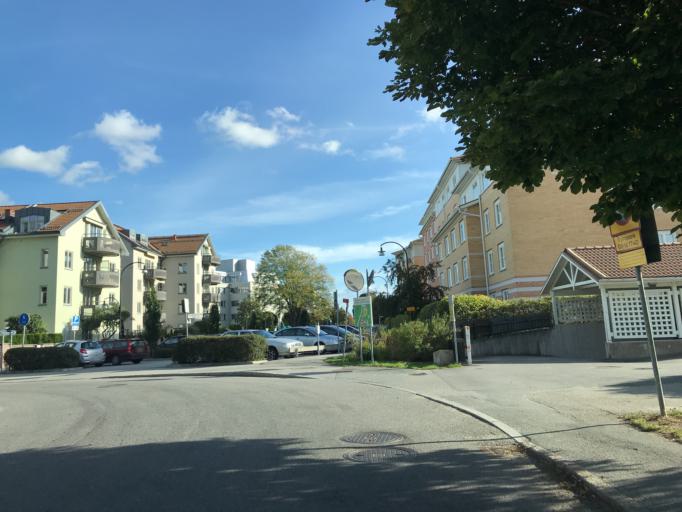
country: SE
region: Stockholm
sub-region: Sollentuna Kommun
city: Sollentuna
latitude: 59.4313
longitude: 17.9403
